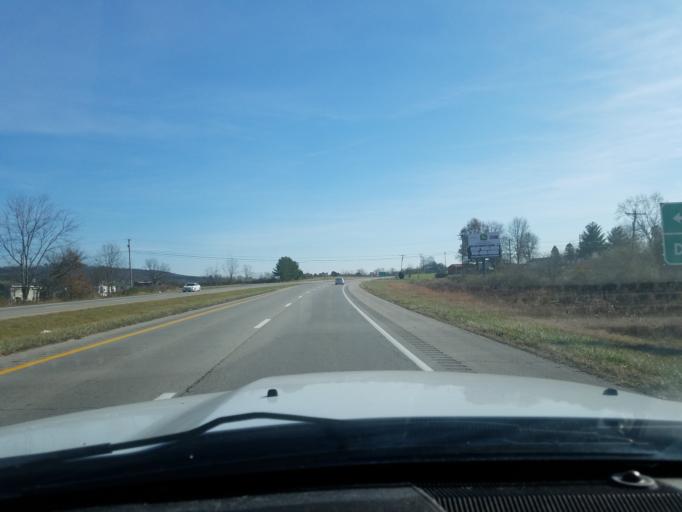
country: US
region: Ohio
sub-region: Pike County
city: Piketon
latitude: 39.0527
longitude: -82.9271
